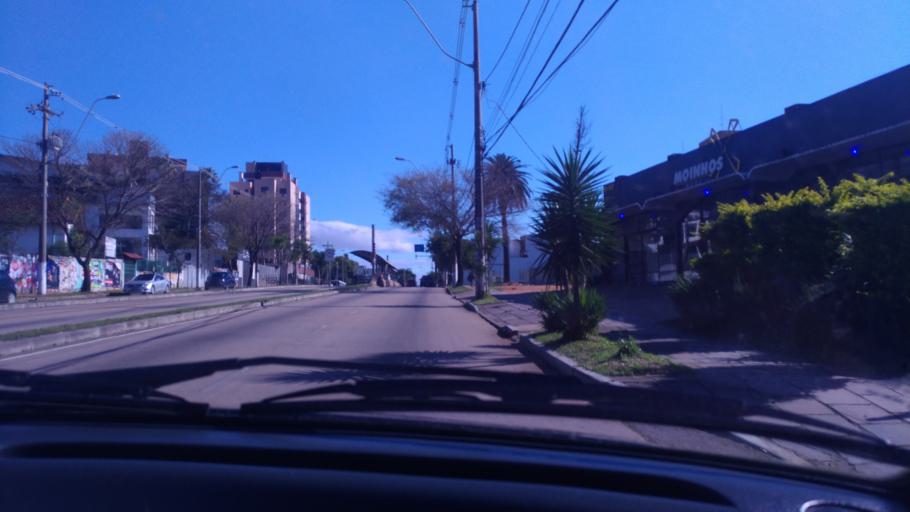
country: BR
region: Rio Grande do Sul
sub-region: Porto Alegre
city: Porto Alegre
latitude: -30.0718
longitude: -51.1916
